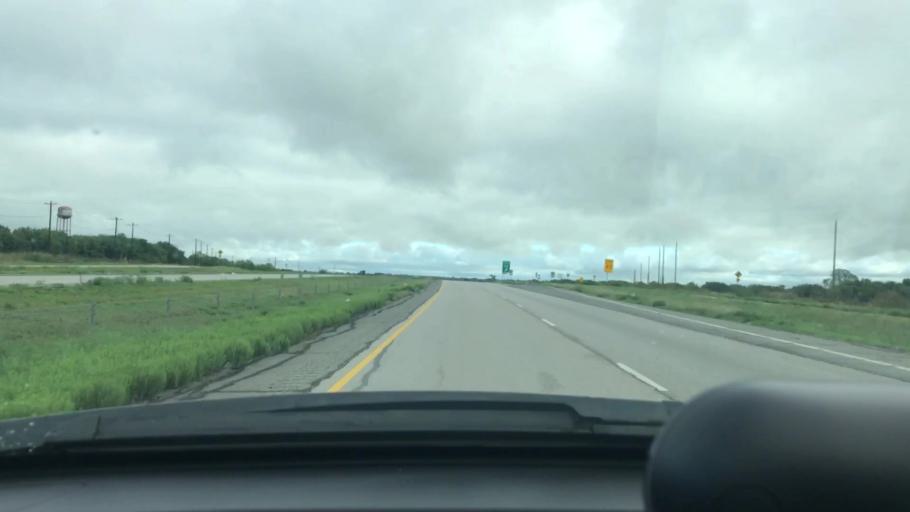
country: US
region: Texas
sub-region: Collin County
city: Anna
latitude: 33.3773
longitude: -96.5808
